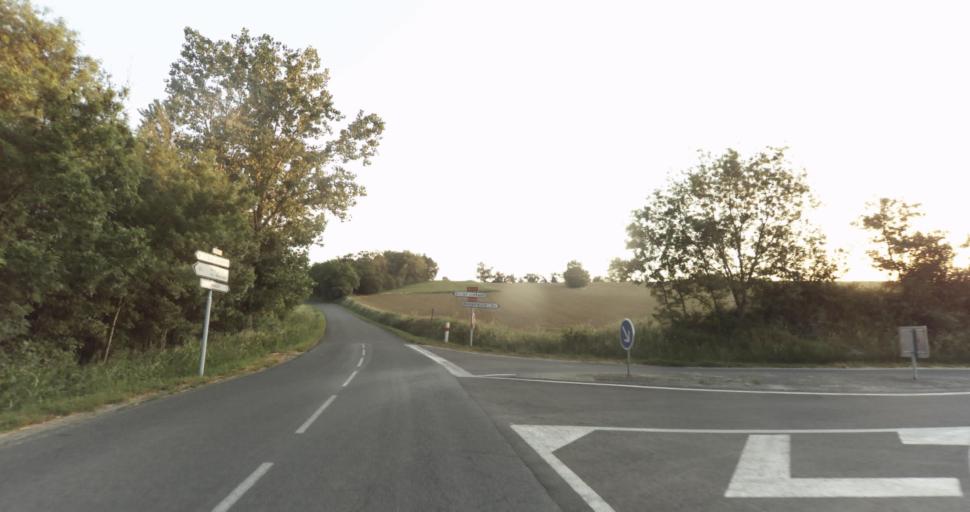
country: FR
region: Midi-Pyrenees
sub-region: Departement du Gers
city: Pujaudran
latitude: 43.6409
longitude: 1.1080
